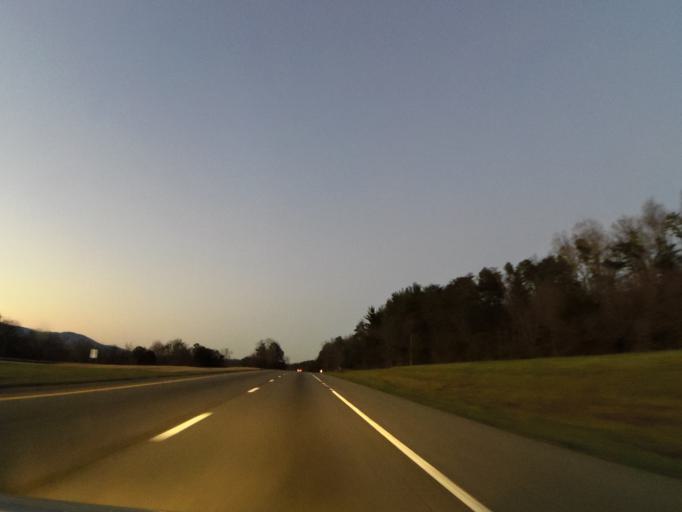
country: US
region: Tennessee
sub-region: Cocke County
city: Newport
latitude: 35.8642
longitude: -83.1839
